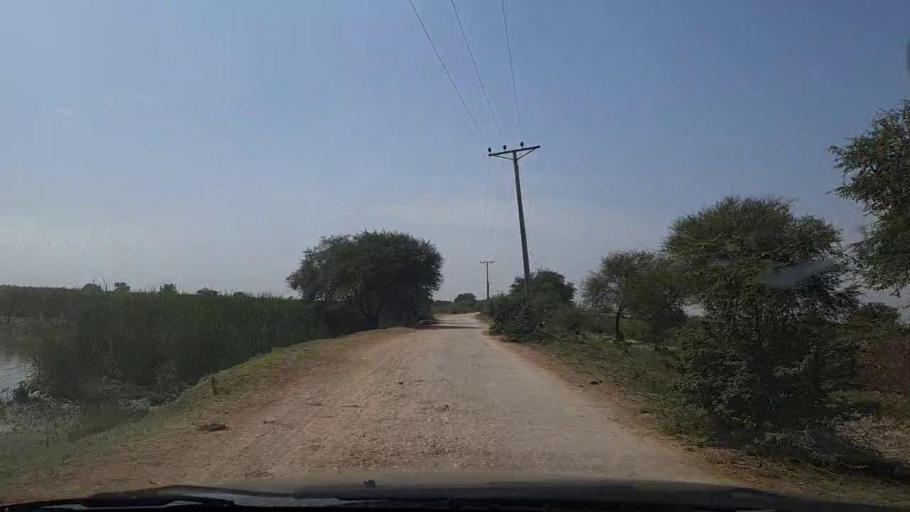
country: PK
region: Sindh
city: Mirpur Batoro
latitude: 24.6088
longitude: 68.2452
